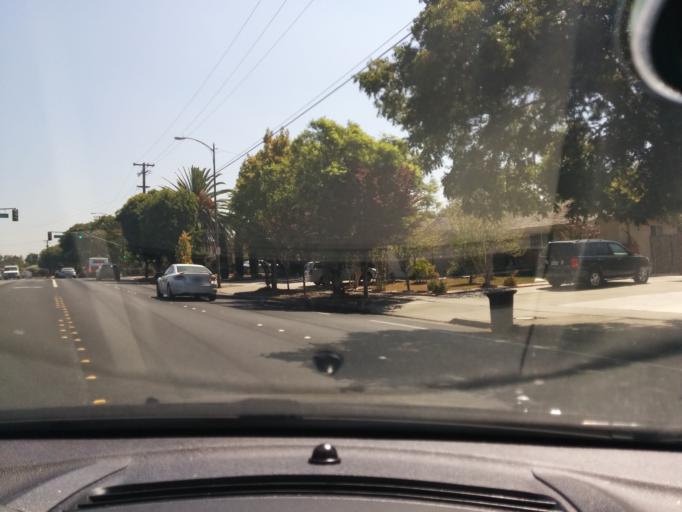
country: US
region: California
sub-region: Santa Clara County
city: Cupertino
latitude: 37.3102
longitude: -122.0242
